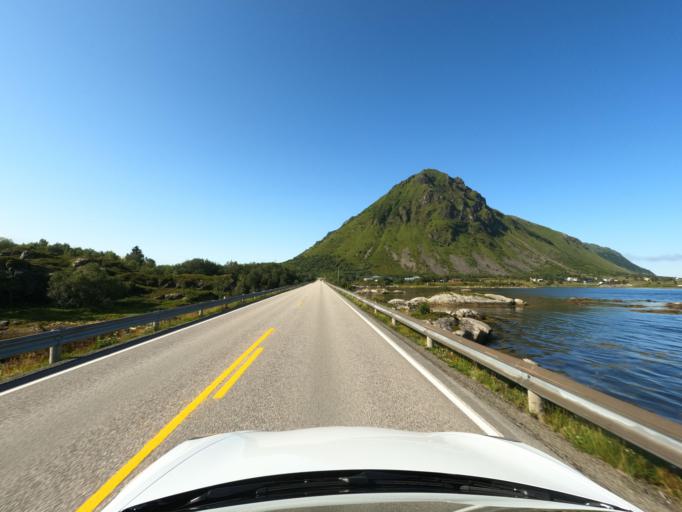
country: NO
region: Nordland
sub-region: Vestvagoy
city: Evjen
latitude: 68.2688
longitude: 13.9756
